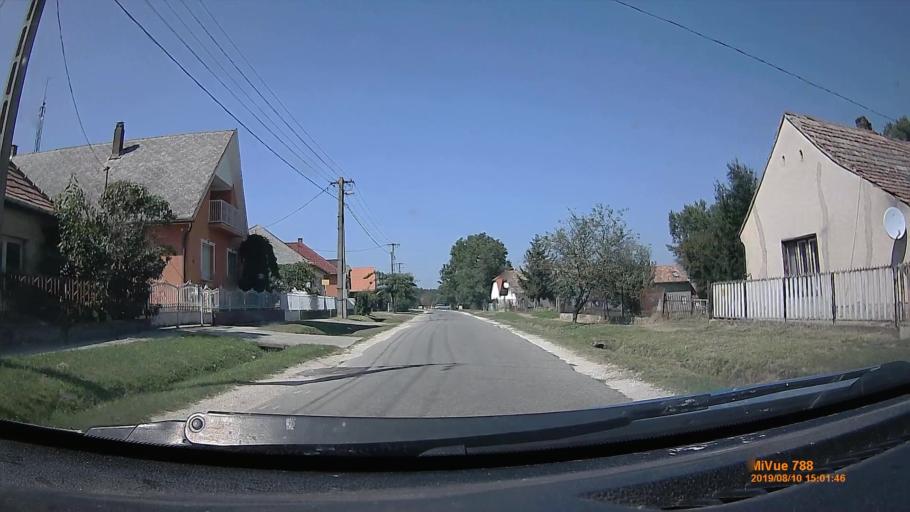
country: HU
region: Somogy
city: Lengyeltoti
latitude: 46.6514
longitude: 17.5769
